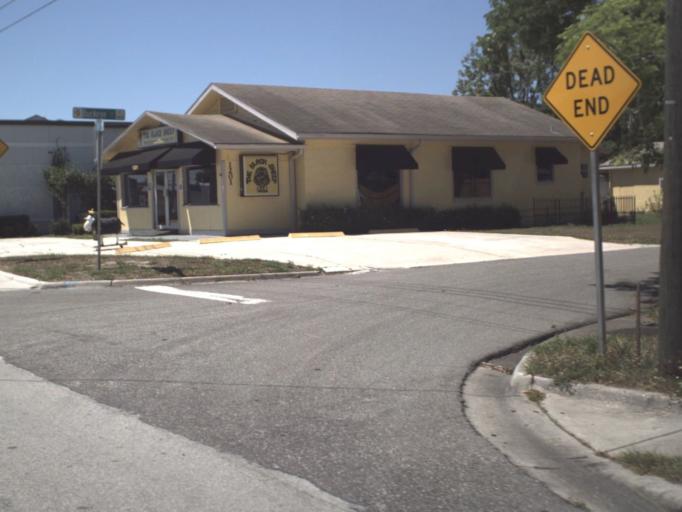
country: US
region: Florida
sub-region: Orange County
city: Fairview Shores
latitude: 28.5966
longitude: -81.3964
